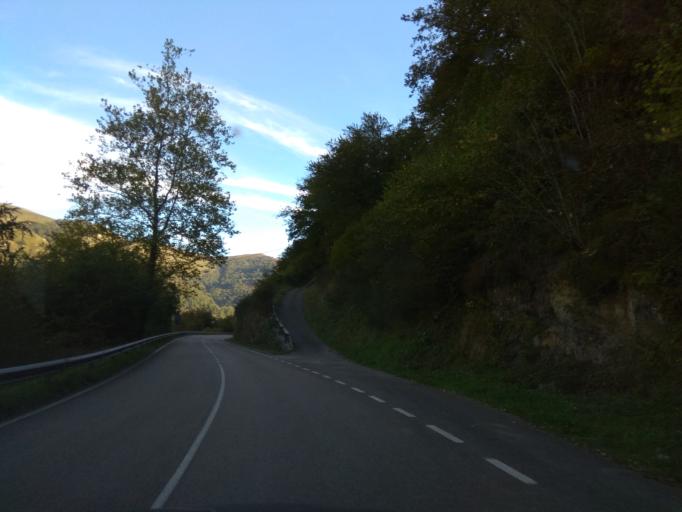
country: ES
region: Cantabria
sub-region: Provincia de Cantabria
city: Ruente
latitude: 43.2057
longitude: -4.3641
